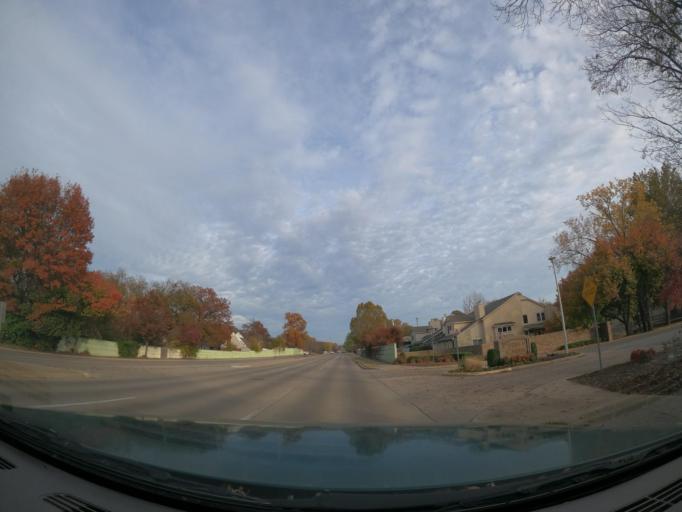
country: US
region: Oklahoma
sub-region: Tulsa County
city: Jenks
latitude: 36.0608
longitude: -95.9374
